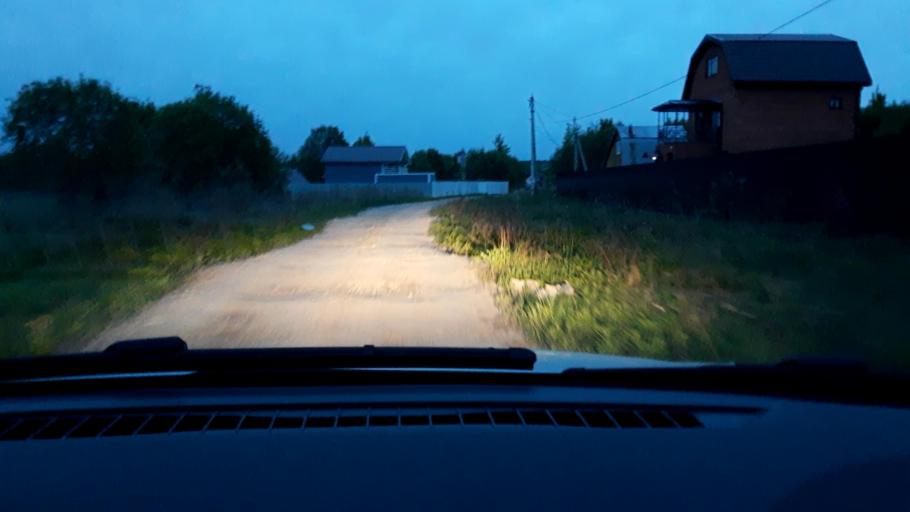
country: RU
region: Nizjnij Novgorod
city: Afonino
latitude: 56.2603
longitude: 44.0794
